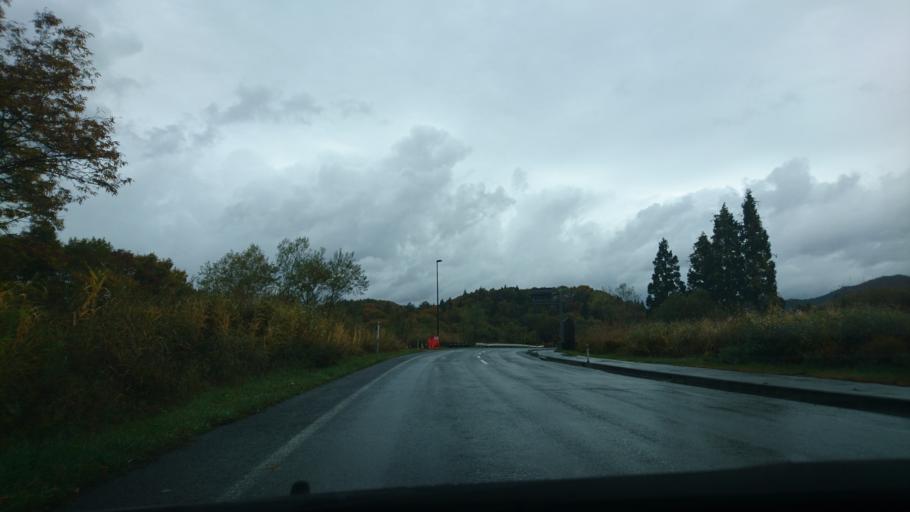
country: JP
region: Akita
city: Yokotemachi
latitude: 39.3574
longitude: 140.7615
